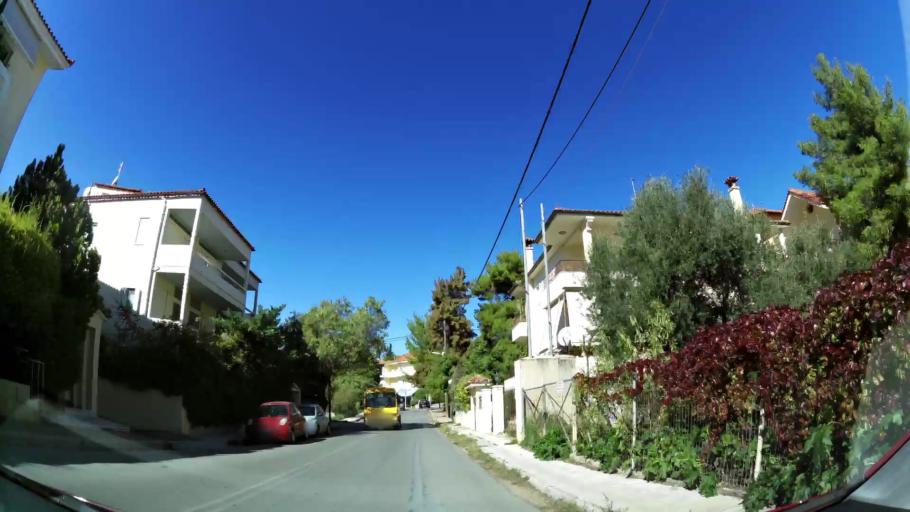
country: GR
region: Attica
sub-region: Nomarchia Anatolikis Attikis
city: Leondarion
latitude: 37.9835
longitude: 23.8562
